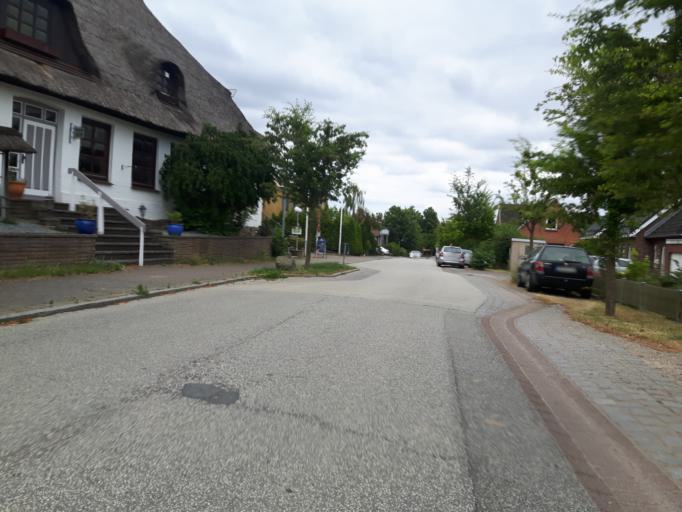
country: DE
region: Schleswig-Holstein
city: Schashagen
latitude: 54.1321
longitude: 10.9085
